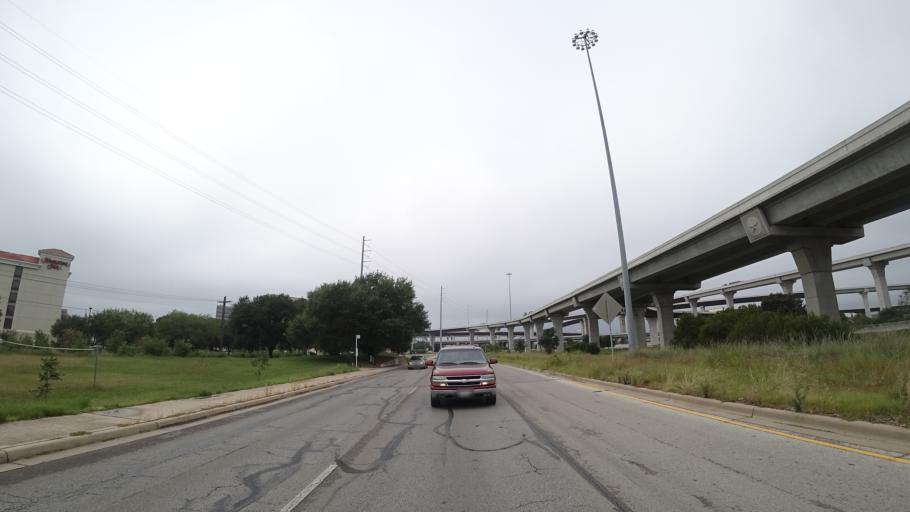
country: US
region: Texas
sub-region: Travis County
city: Austin
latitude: 30.2157
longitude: -97.7484
